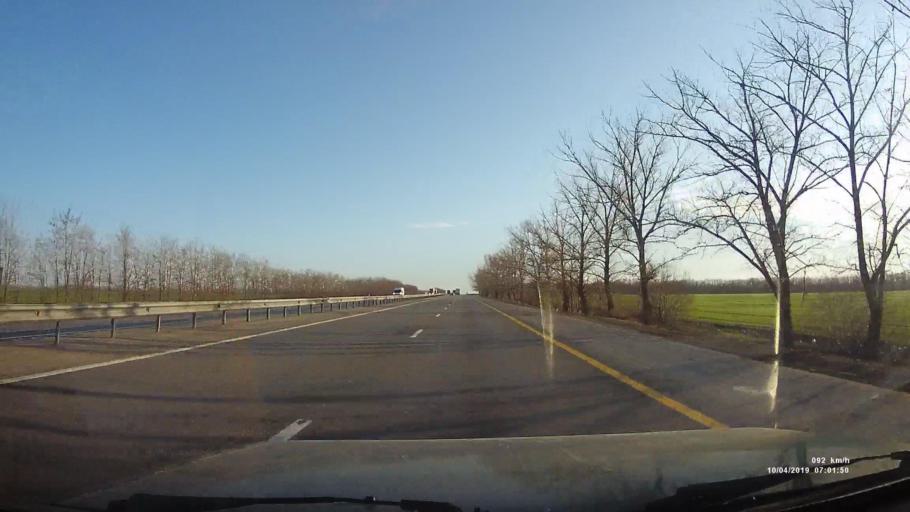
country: RU
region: Rostov
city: Krasyukovskaya
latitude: 47.6001
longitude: 39.9879
